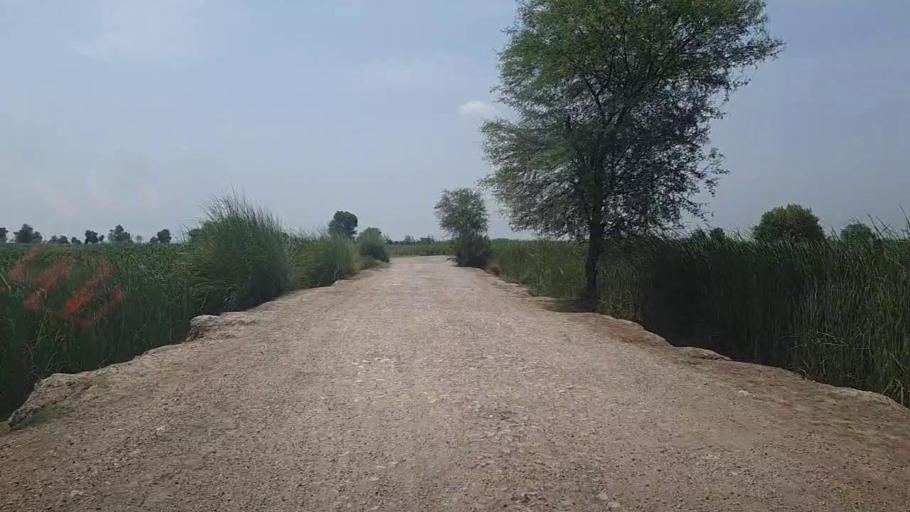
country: PK
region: Sindh
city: Ubauro
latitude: 28.1619
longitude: 69.8286
